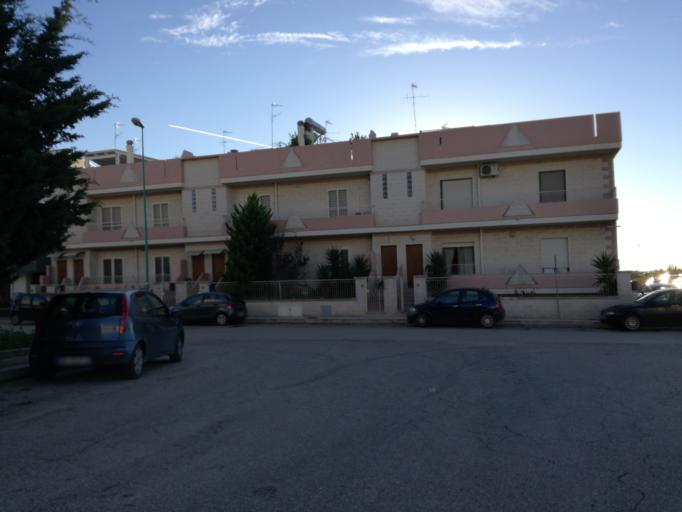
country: IT
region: Apulia
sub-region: Provincia di Bari
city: Adelfia
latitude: 41.0076
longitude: 16.8635
